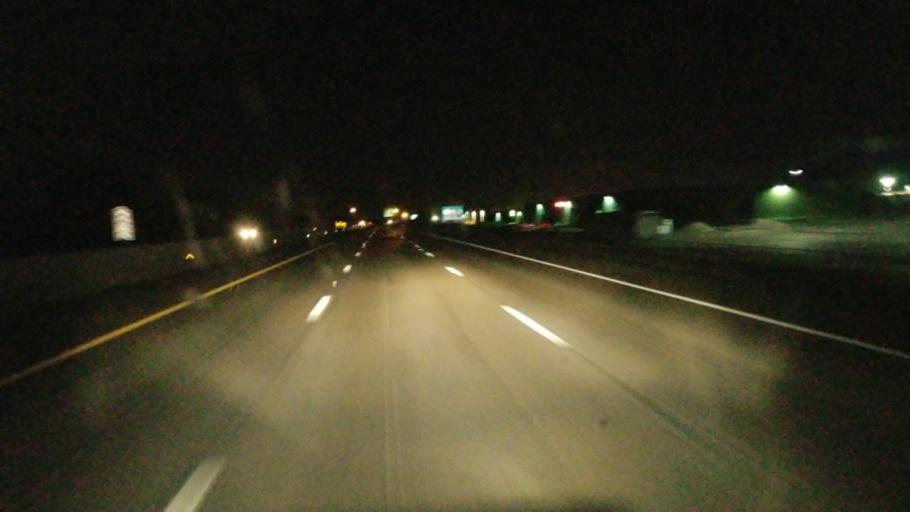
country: US
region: Ohio
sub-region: Montgomery County
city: Huber Heights
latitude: 39.8689
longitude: -84.1191
